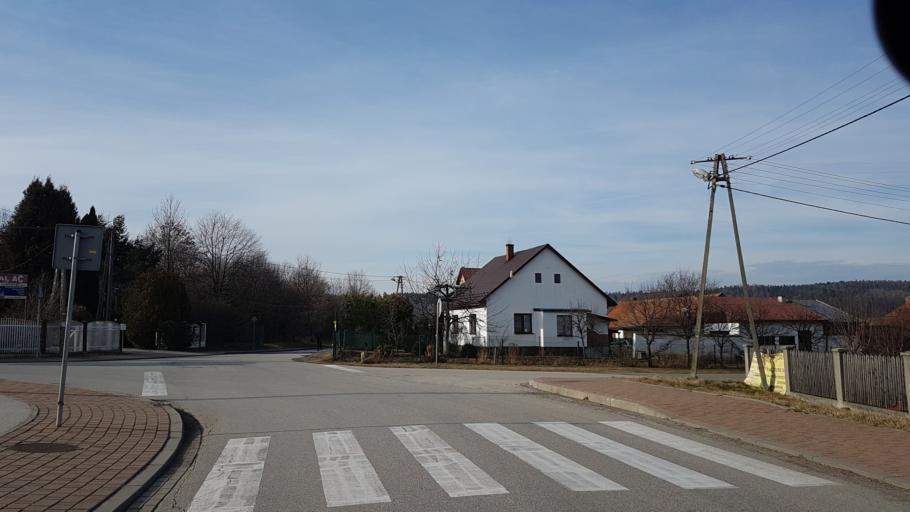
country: PL
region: Lesser Poland Voivodeship
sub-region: Powiat nowosadecki
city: Stary Sacz
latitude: 49.5433
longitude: 20.6309
